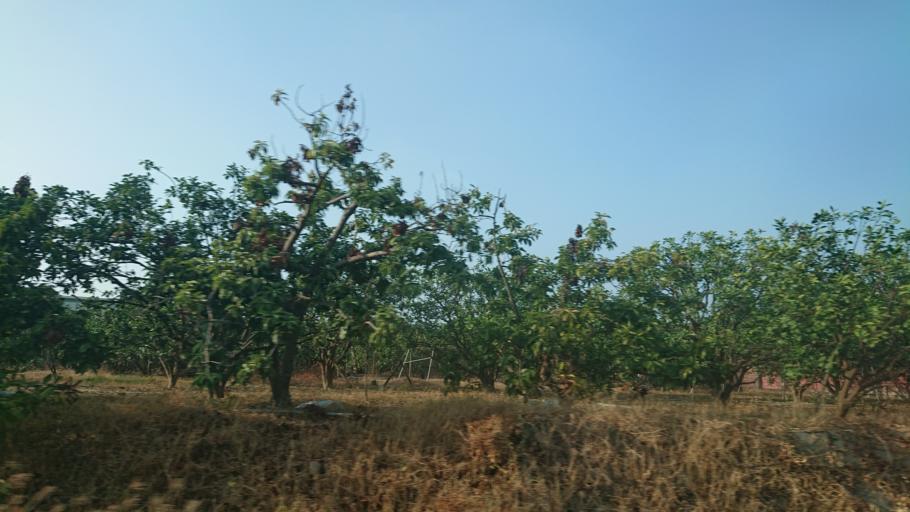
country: TW
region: Taiwan
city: Xinying
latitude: 23.1744
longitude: 120.2587
